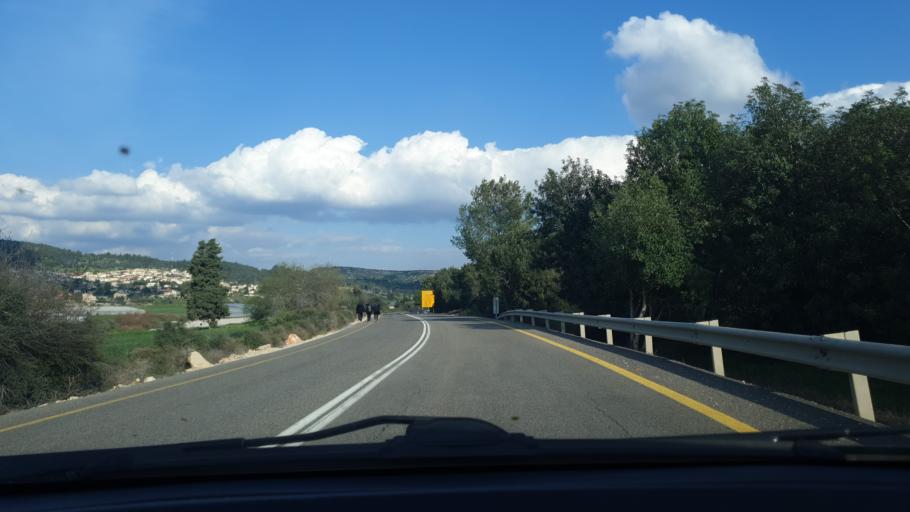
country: IL
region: Jerusalem
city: Bet Shemesh
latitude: 31.7042
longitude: 34.9328
